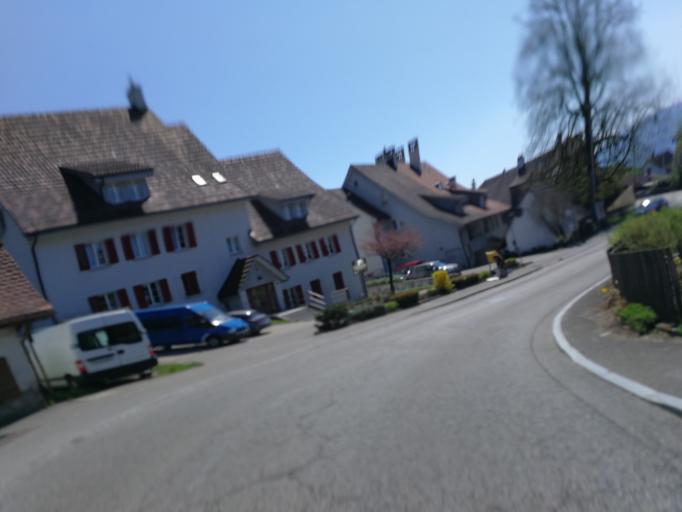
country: CH
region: Zurich
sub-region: Bezirk Meilen
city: Herrliberg
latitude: 47.2950
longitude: 8.6319
